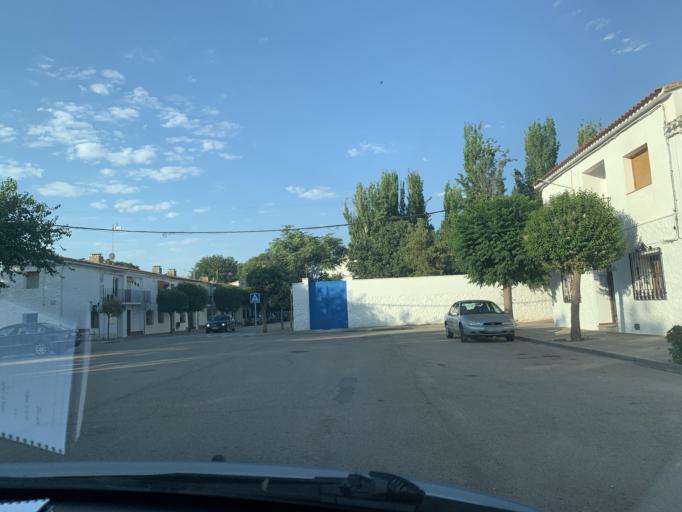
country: ES
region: Castille-La Mancha
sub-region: Provincia de Ciudad Real
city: Argamasilla de Alba
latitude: 39.1740
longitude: -3.2362
